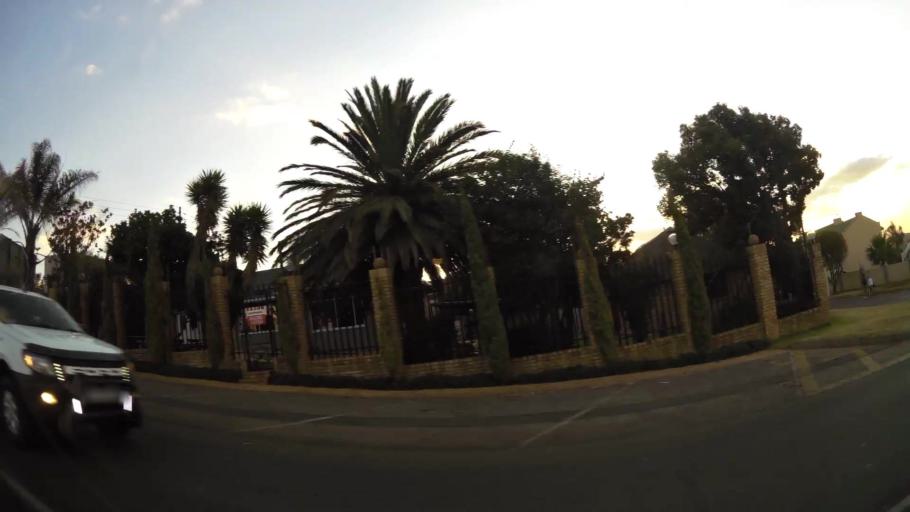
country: ZA
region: Gauteng
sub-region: West Rand District Municipality
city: Krugersdorp
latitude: -26.0757
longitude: 27.7888
